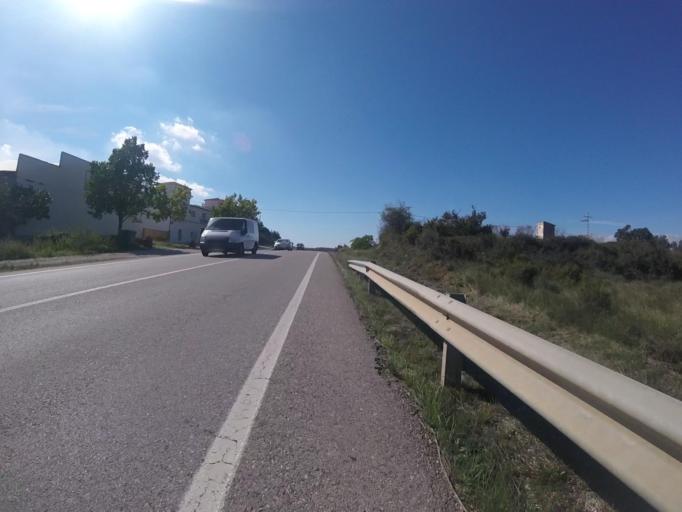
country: ES
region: Valencia
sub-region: Provincia de Castello
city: Albocasser
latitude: 40.3362
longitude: -0.0120
